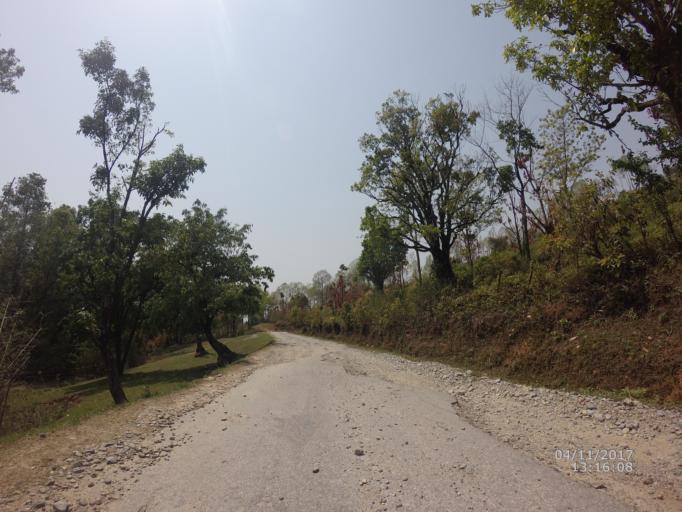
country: NP
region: Western Region
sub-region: Gandaki Zone
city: Pokhara
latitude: 28.2091
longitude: 84.0388
